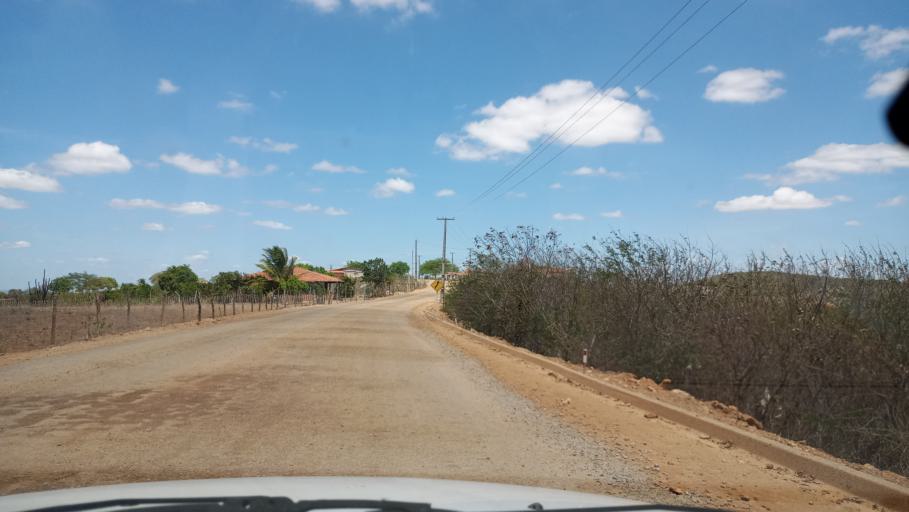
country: BR
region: Rio Grande do Norte
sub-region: Sao Paulo Do Potengi
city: Sao Paulo do Potengi
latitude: -5.7832
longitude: -35.9151
